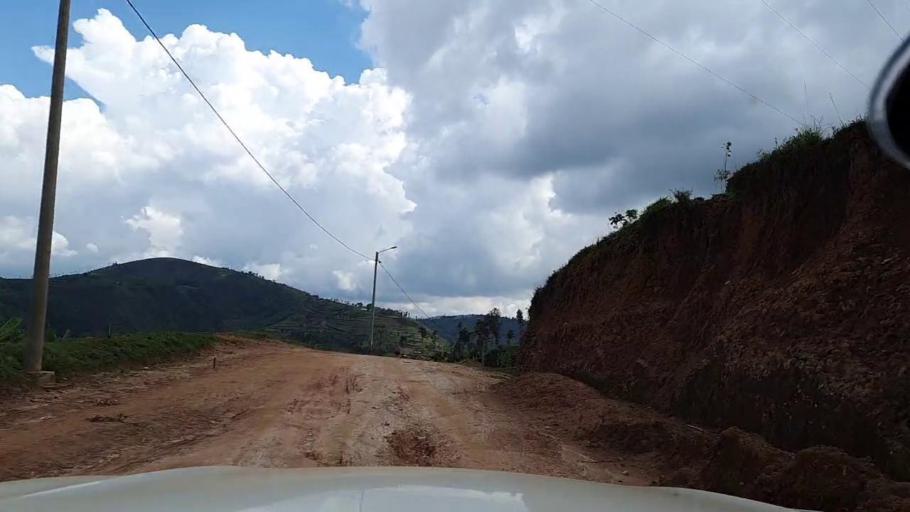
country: RW
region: Southern Province
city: Nzega
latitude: -2.6917
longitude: 29.4433
